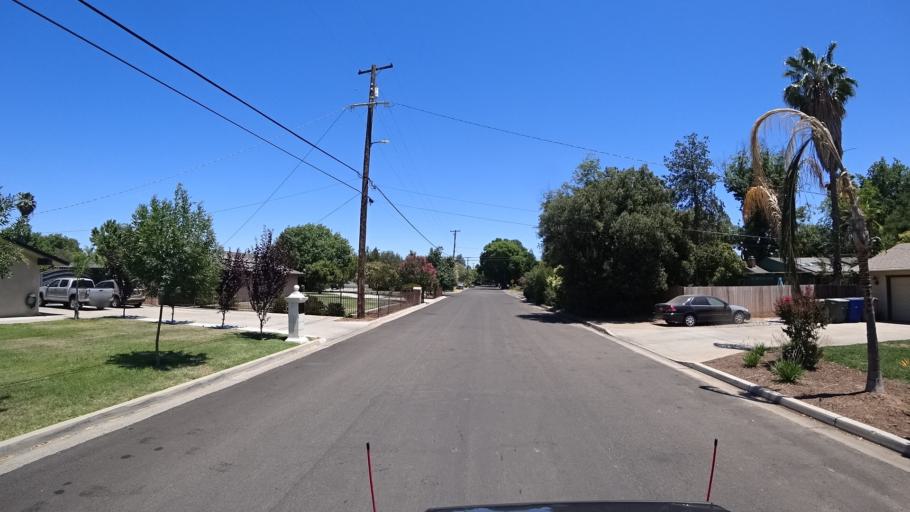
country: US
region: California
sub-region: Fresno County
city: Tarpey Village
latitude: 36.8050
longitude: -119.7504
